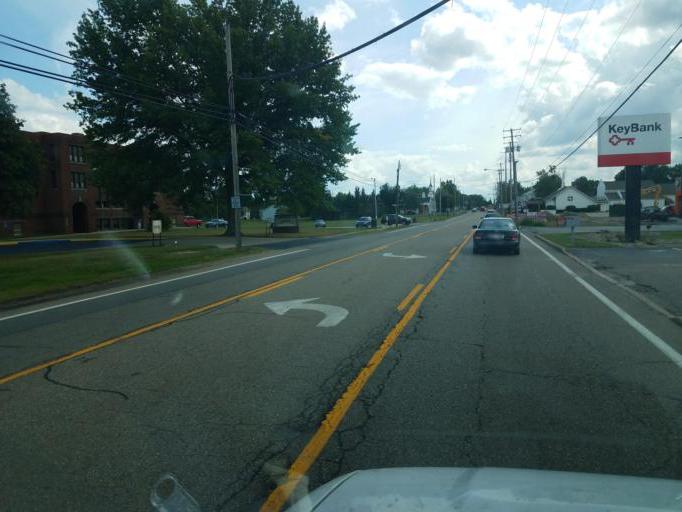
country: US
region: Ohio
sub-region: Portage County
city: Ravenna
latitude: 41.1018
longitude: -81.2426
